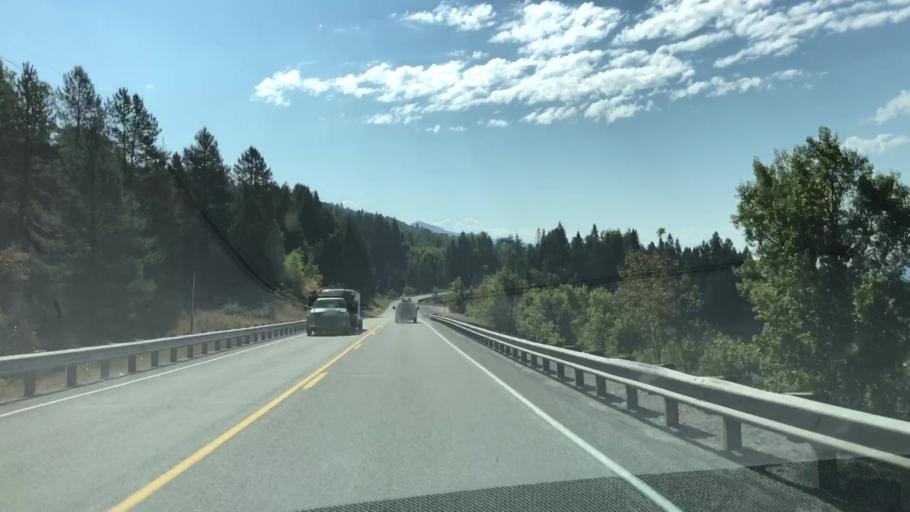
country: US
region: Idaho
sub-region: Teton County
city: Victor
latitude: 43.3023
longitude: -111.1325
